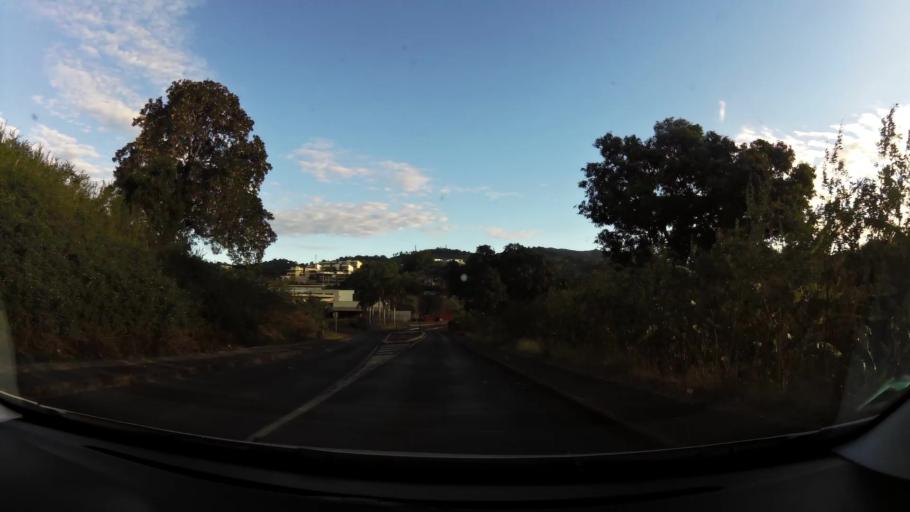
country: YT
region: Koungou
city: Koungou
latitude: -12.7333
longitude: 45.2025
